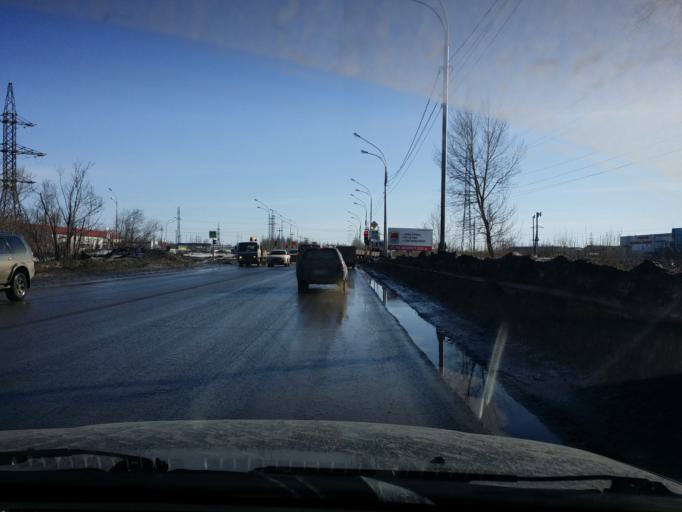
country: RU
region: Khanty-Mansiyskiy Avtonomnyy Okrug
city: Nizhnevartovsk
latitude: 60.9312
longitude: 76.5312
